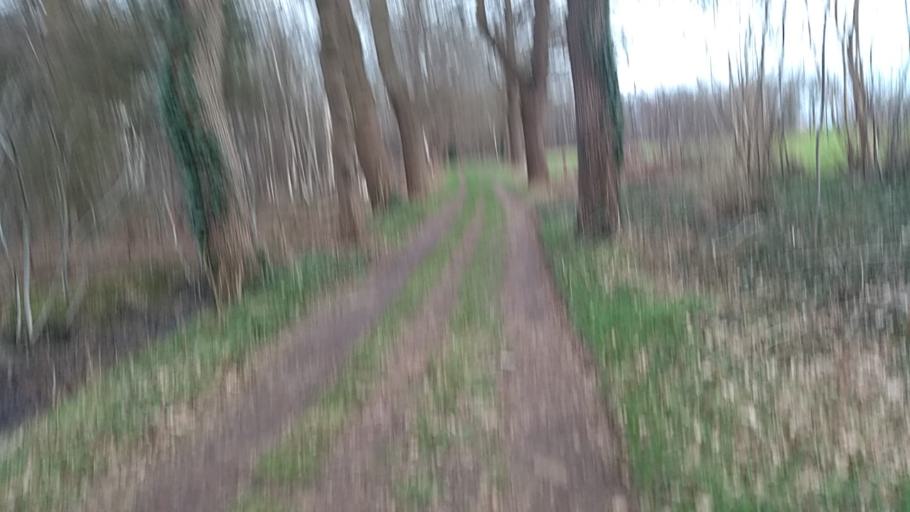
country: NL
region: Overijssel
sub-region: Gemeente Almelo
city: Almelo
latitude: 52.3581
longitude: 6.7105
